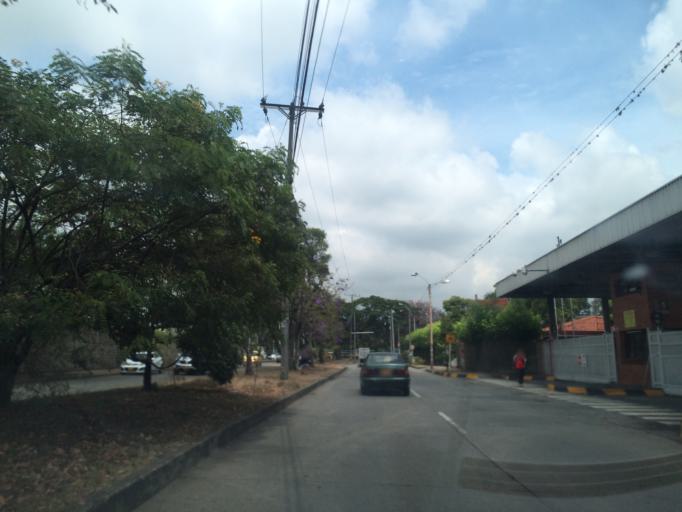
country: CO
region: Valle del Cauca
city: Cali
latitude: 3.3709
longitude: -76.5280
